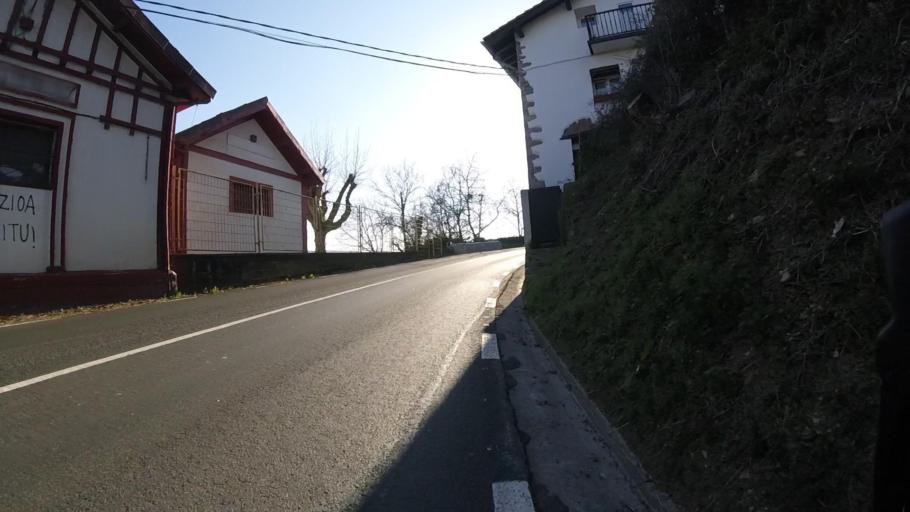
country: ES
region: Basque Country
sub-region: Provincia de Guipuzcoa
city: Errenteria
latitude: 43.2888
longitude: -1.9073
